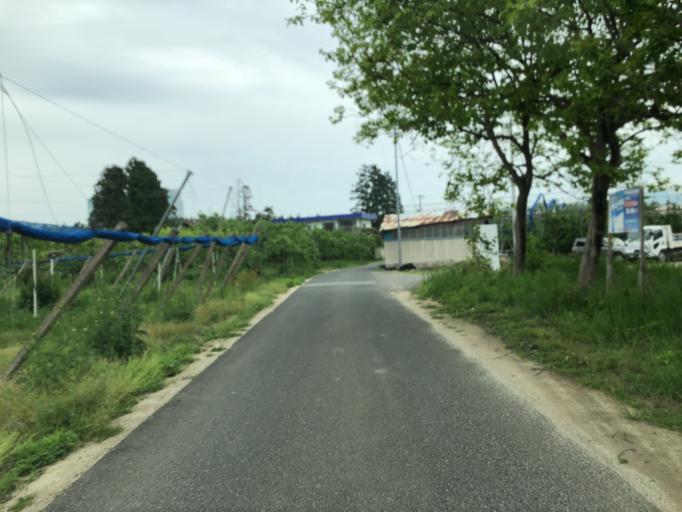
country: JP
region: Fukushima
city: Fukushima-shi
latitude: 37.8000
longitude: 140.4519
